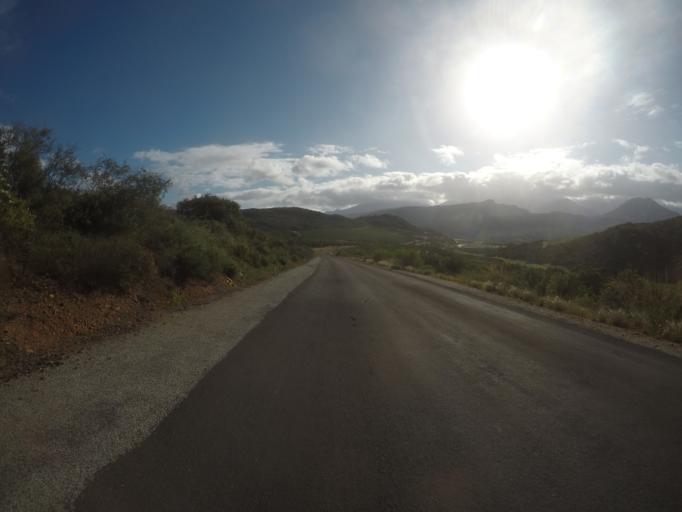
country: ZA
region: Western Cape
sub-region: West Coast District Municipality
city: Clanwilliam
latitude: -32.4334
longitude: 18.9476
